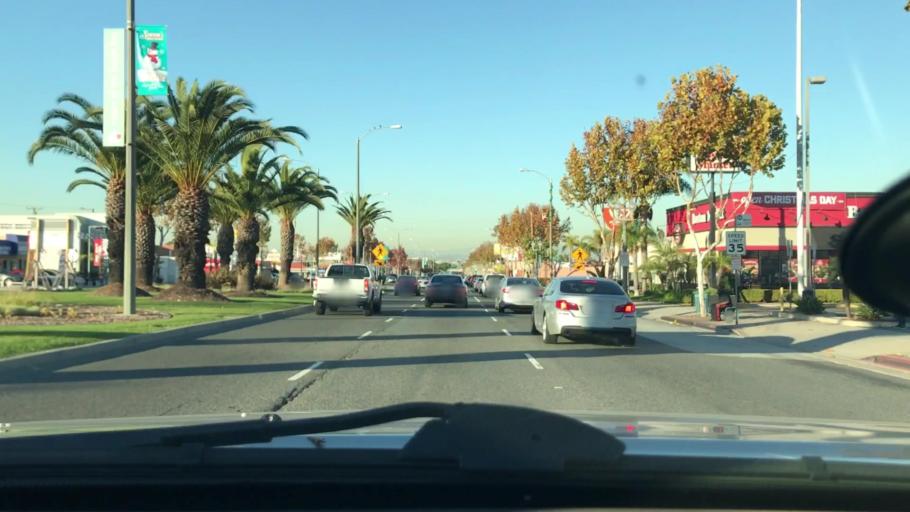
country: US
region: California
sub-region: Los Angeles County
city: Lawndale
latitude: 33.8751
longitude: -118.3524
